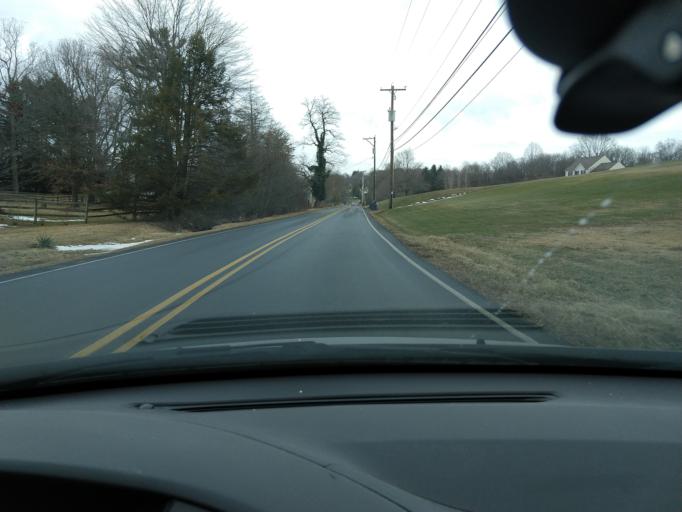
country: US
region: Pennsylvania
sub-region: Chester County
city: South Pottstown
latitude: 40.2015
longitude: -75.6765
